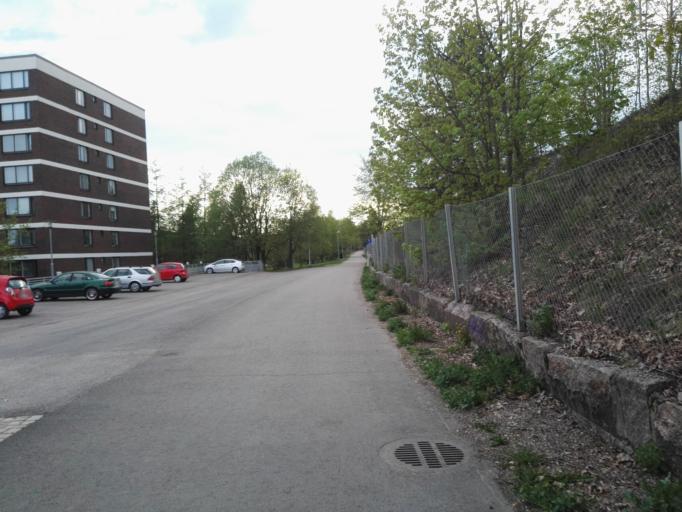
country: FI
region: Paijanne Tavastia
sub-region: Lahti
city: Lahti
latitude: 60.9762
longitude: 25.6535
